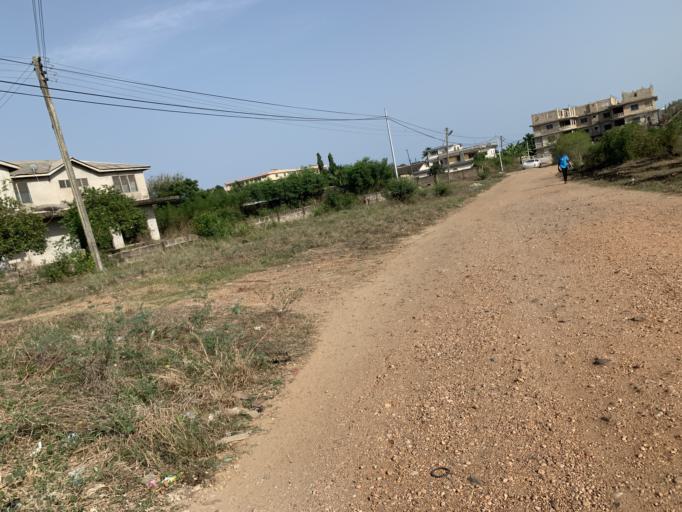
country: GH
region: Central
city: Winneba
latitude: 5.3686
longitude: -0.6406
